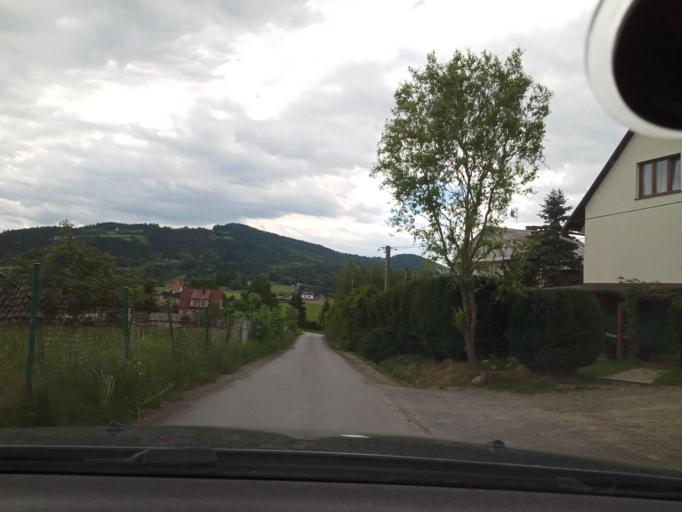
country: PL
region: Lesser Poland Voivodeship
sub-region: Powiat limanowski
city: Tymbark
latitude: 49.7666
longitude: 20.3365
